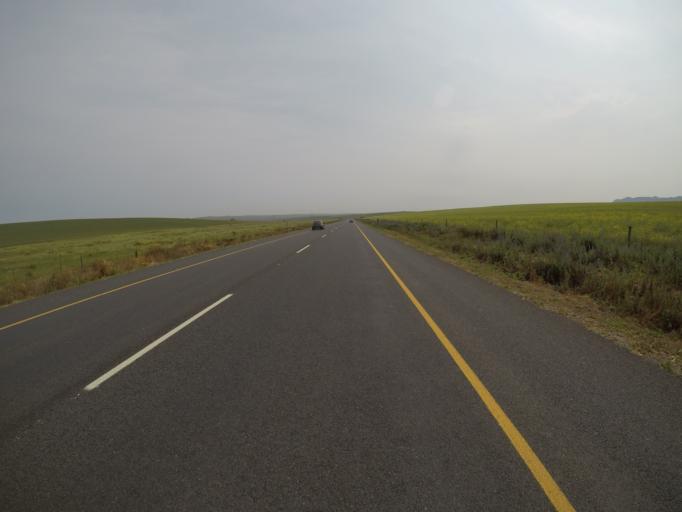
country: ZA
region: Western Cape
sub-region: West Coast District Municipality
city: Malmesbury
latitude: -33.4654
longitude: 18.7895
